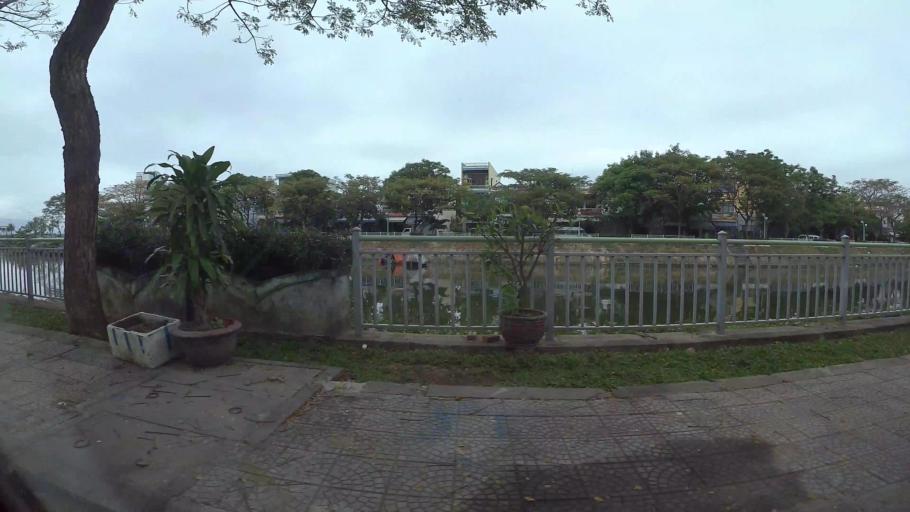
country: VN
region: Da Nang
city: Thanh Khe
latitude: 16.0737
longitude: 108.1787
